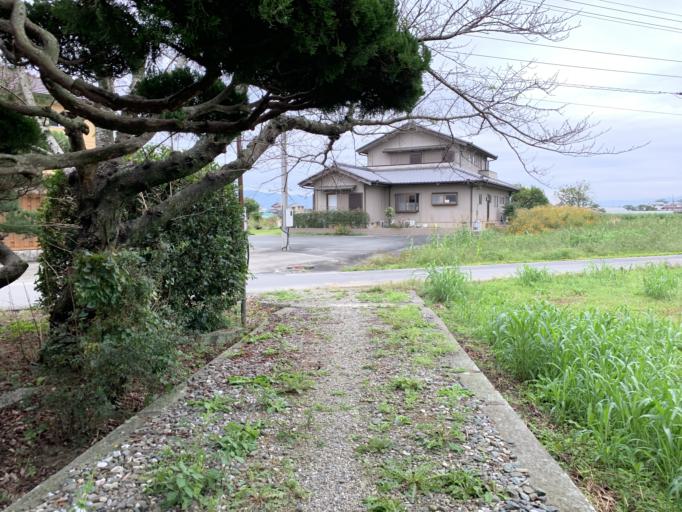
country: JP
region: Tokushima
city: Ishii
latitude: 34.0899
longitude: 134.4464
